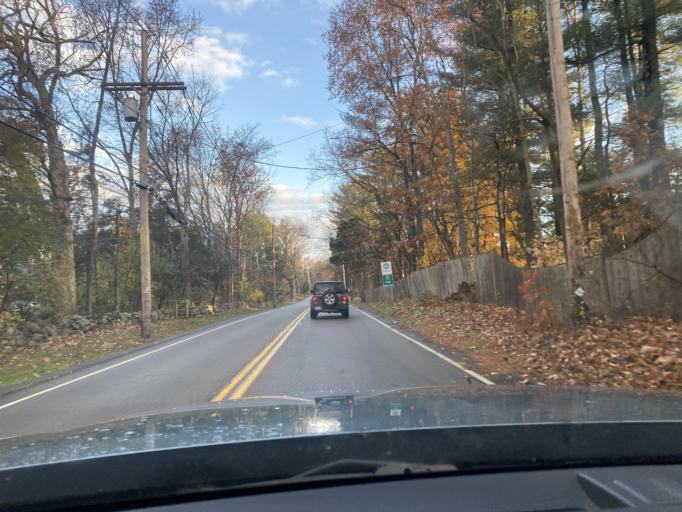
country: US
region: Massachusetts
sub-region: Norfolk County
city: Needham
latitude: 42.2606
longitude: -71.2371
